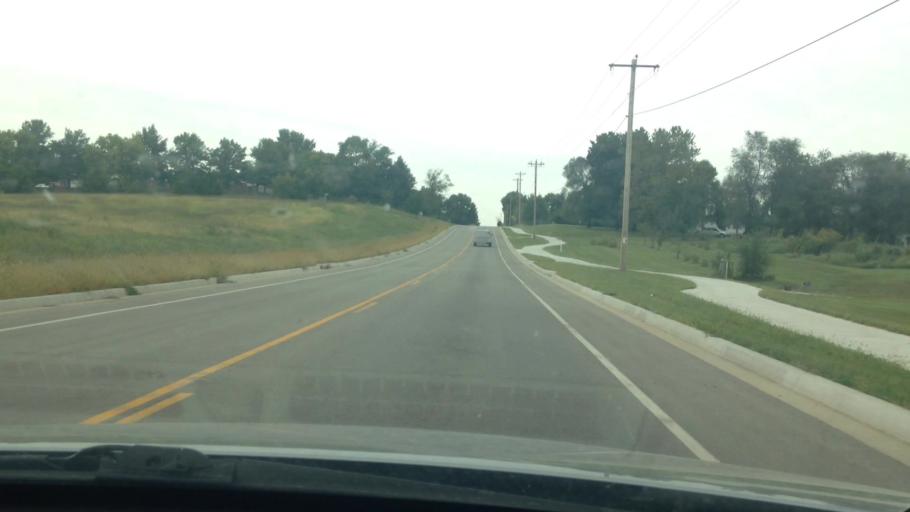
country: US
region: Missouri
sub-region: Platte County
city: Platte City
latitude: 39.3445
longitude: -94.7793
